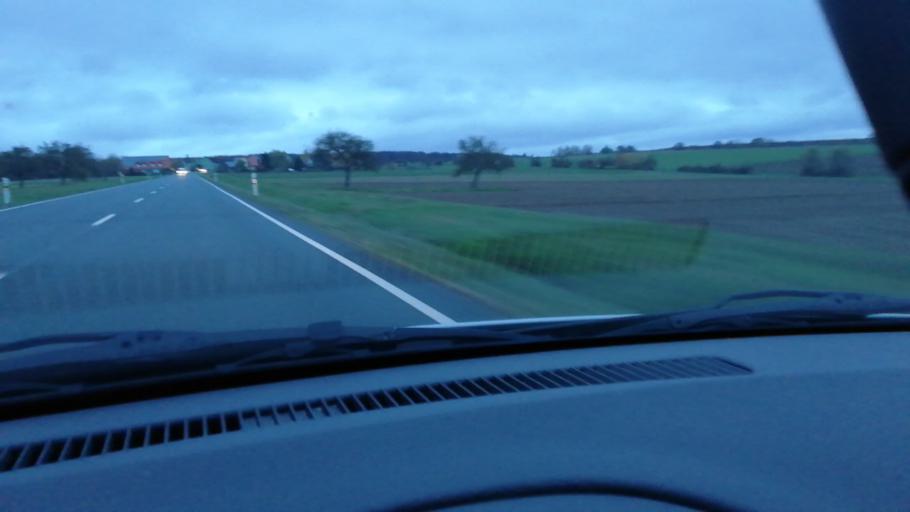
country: DE
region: Bavaria
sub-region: Regierungsbezirk Unterfranken
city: Bischbrunn
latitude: 49.8708
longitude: 9.5006
